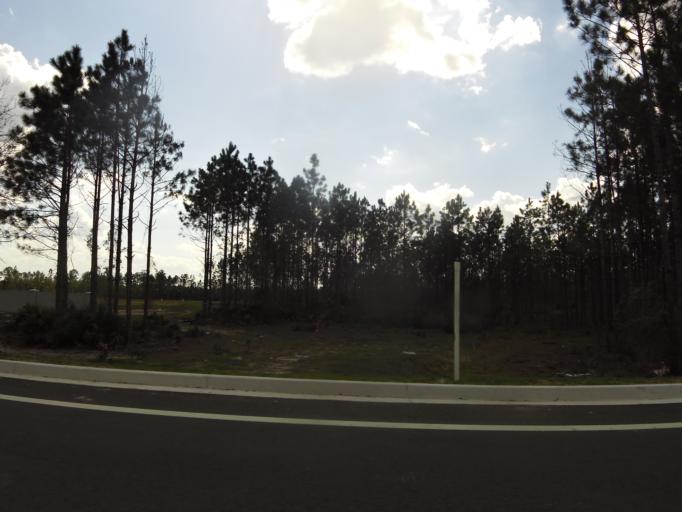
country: US
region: Florida
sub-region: Saint Johns County
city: Palm Valley
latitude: 30.1944
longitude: -81.5066
